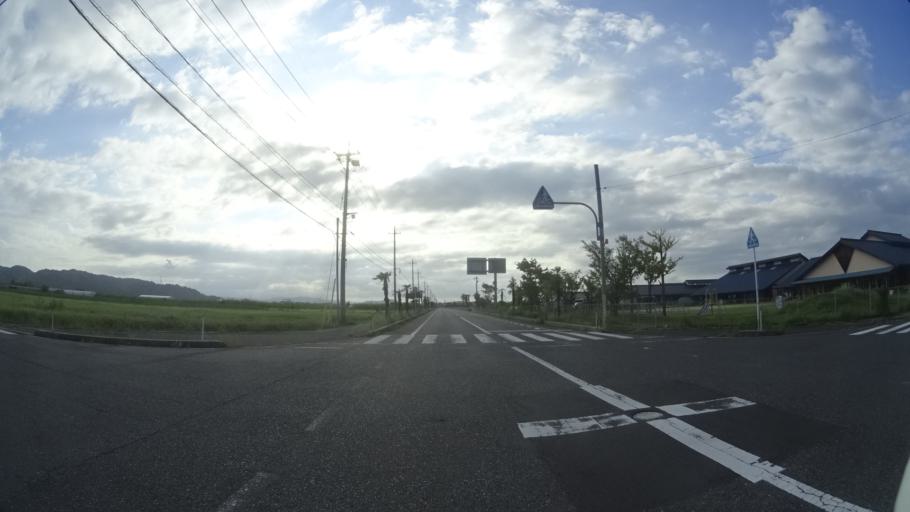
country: JP
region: Tottori
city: Kurayoshi
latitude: 35.4912
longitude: 133.8794
